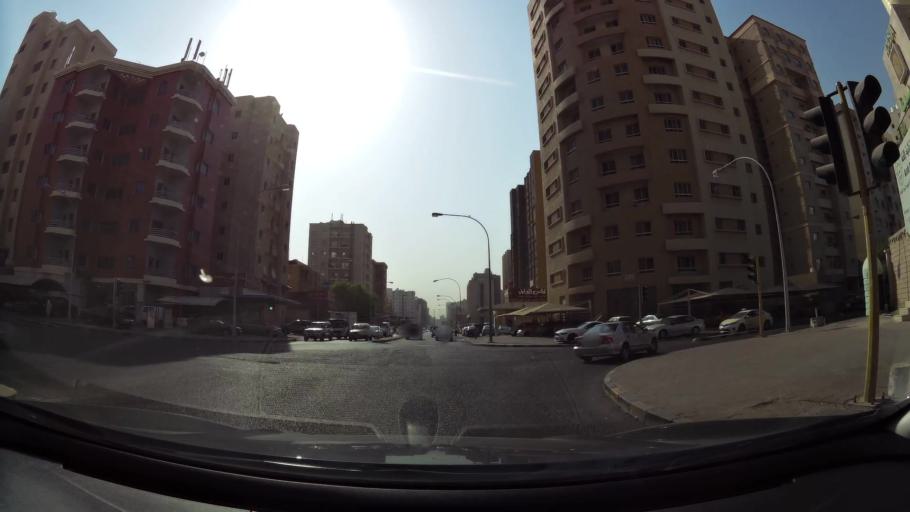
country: KW
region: Muhafazat Hawalli
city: Hawalli
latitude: 29.3354
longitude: 48.0075
